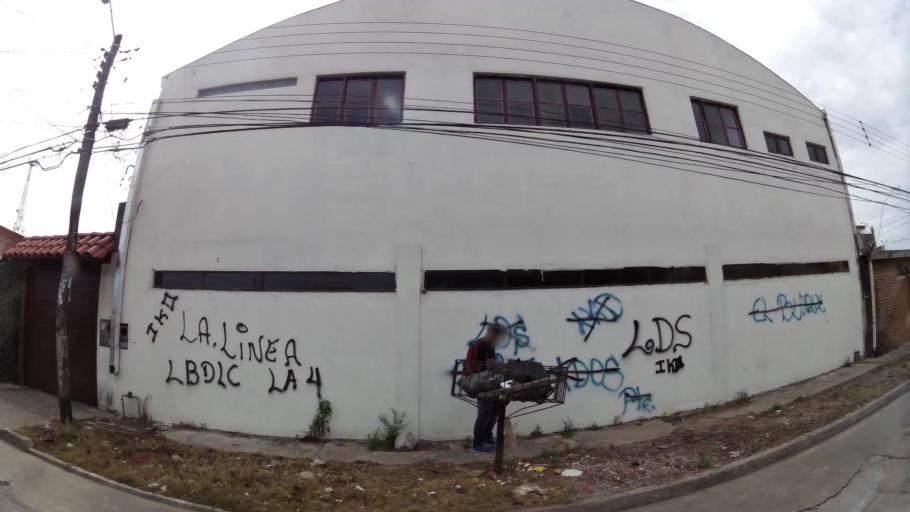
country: BO
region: Santa Cruz
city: Santa Cruz de la Sierra
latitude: -17.7794
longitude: -63.2045
